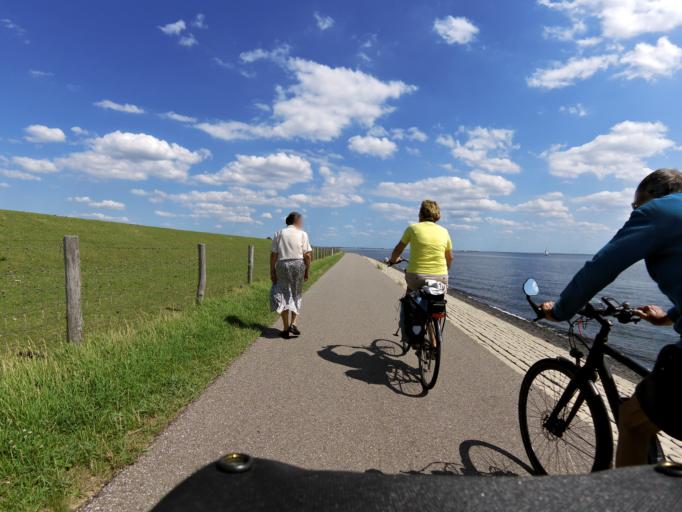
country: NL
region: Zeeland
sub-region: Gemeente Reimerswaal
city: Yerseke
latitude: 51.5240
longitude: 4.1166
